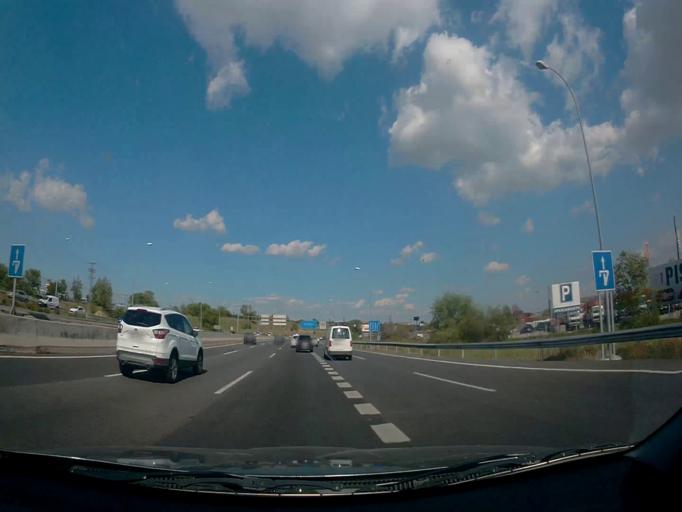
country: ES
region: Madrid
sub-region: Provincia de Madrid
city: Leganes
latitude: 40.3616
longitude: -3.7861
